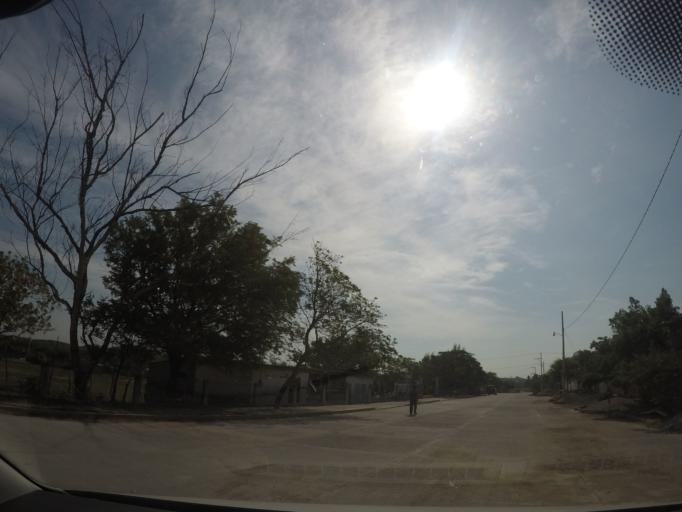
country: MX
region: Oaxaca
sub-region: Salina Cruz
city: Salina Cruz
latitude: 16.2196
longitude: -95.1281
